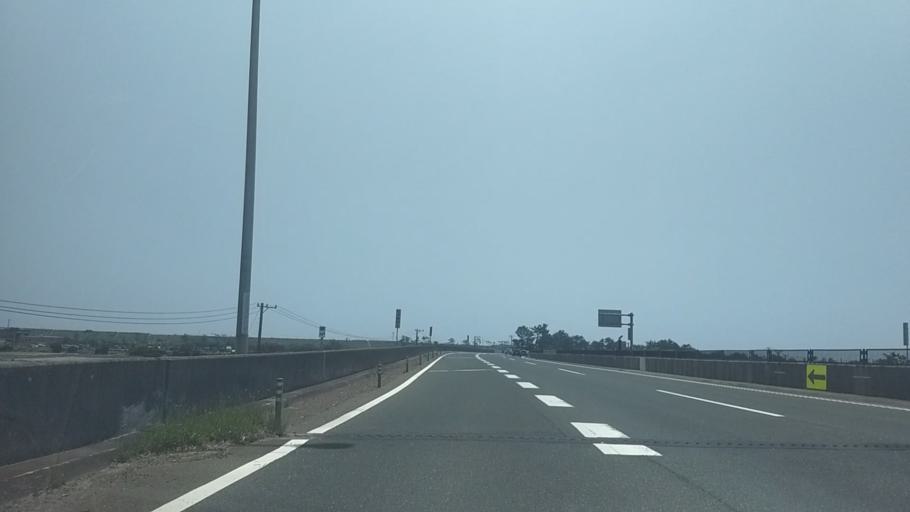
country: JP
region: Shizuoka
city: Hamamatsu
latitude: 34.6789
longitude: 137.6620
